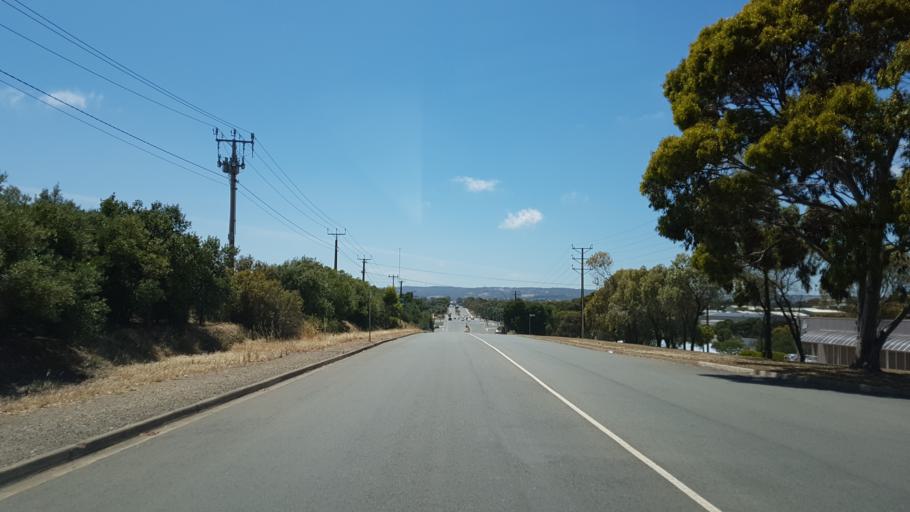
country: AU
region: South Australia
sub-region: Onkaparinga
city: Morphett Vale
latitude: -35.1067
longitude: 138.4946
